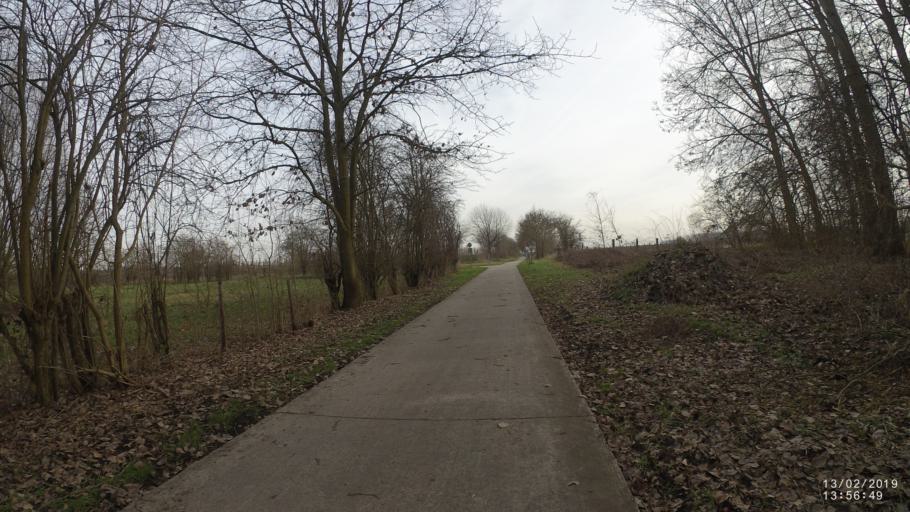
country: BE
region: Flanders
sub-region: Provincie Vlaams-Brabant
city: Zoutleeuw
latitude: 50.8245
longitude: 5.1135
